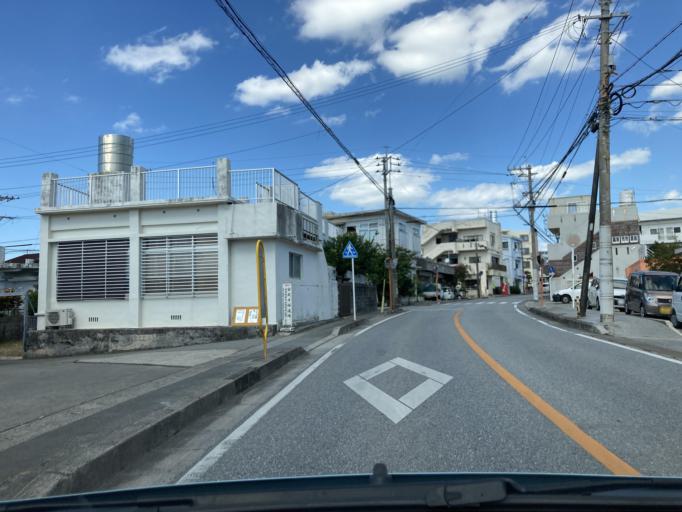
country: JP
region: Okinawa
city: Tomigusuku
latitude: 26.1869
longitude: 127.7274
